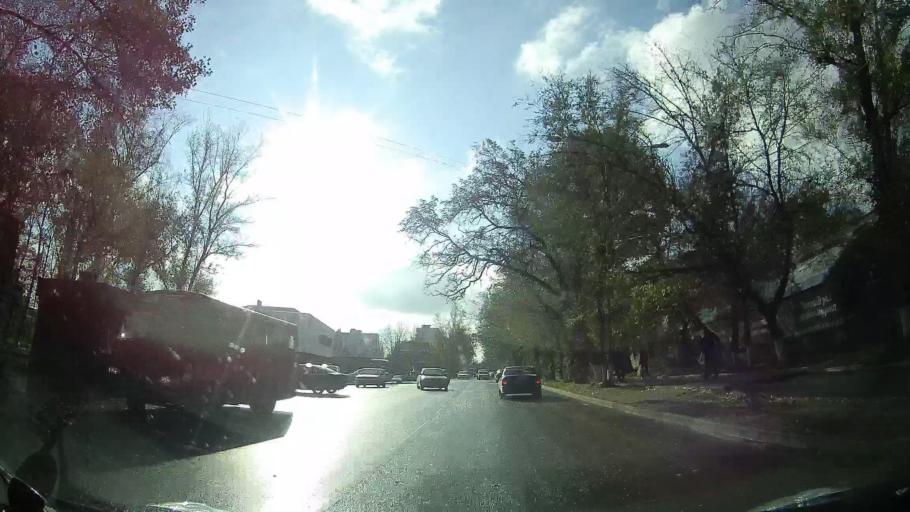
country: RU
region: Rostov
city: Severnyy
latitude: 47.2645
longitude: 39.6663
